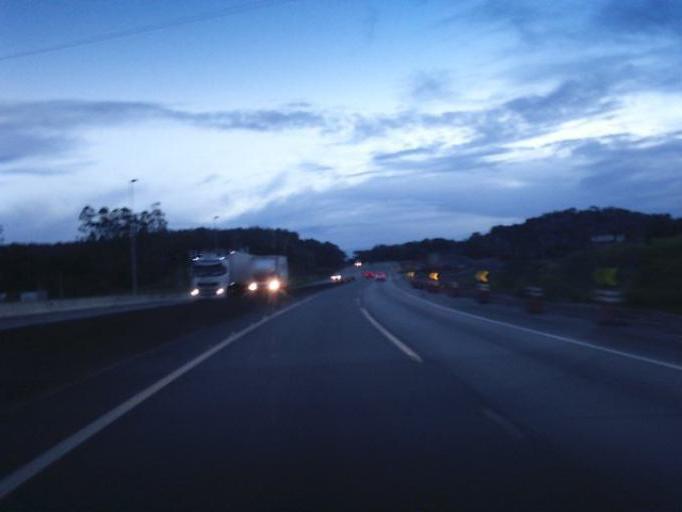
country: BR
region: Santa Catarina
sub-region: Joinville
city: Joinville
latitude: -26.3965
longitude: -48.8391
